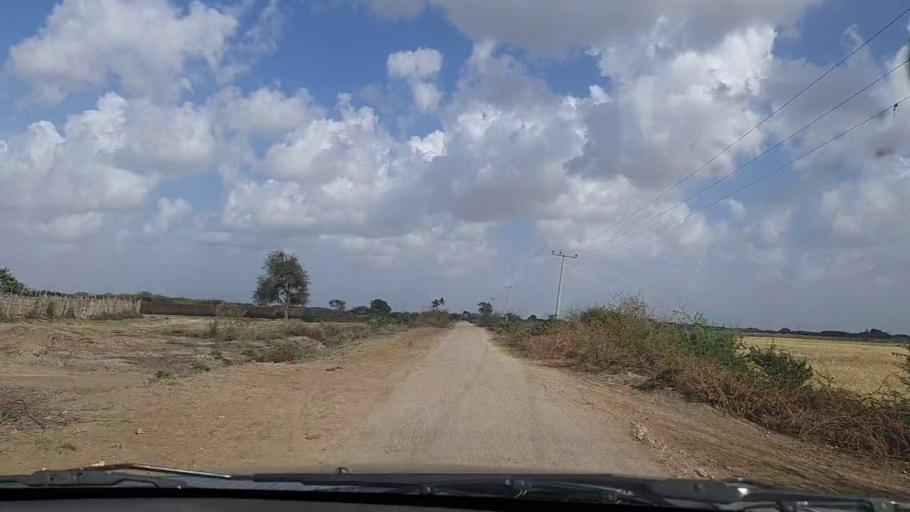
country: PK
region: Sindh
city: Keti Bandar
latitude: 24.0961
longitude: 67.6082
